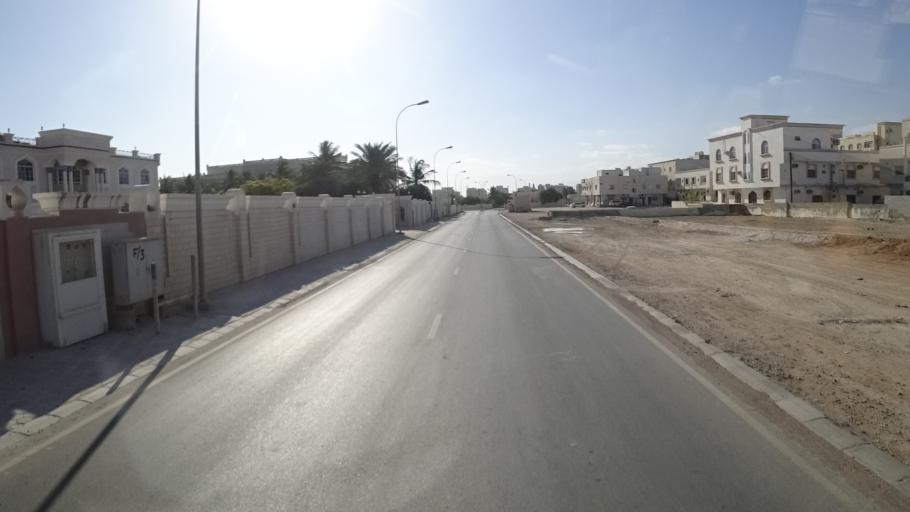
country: OM
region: Zufar
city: Salalah
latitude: 17.0050
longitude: 54.0705
